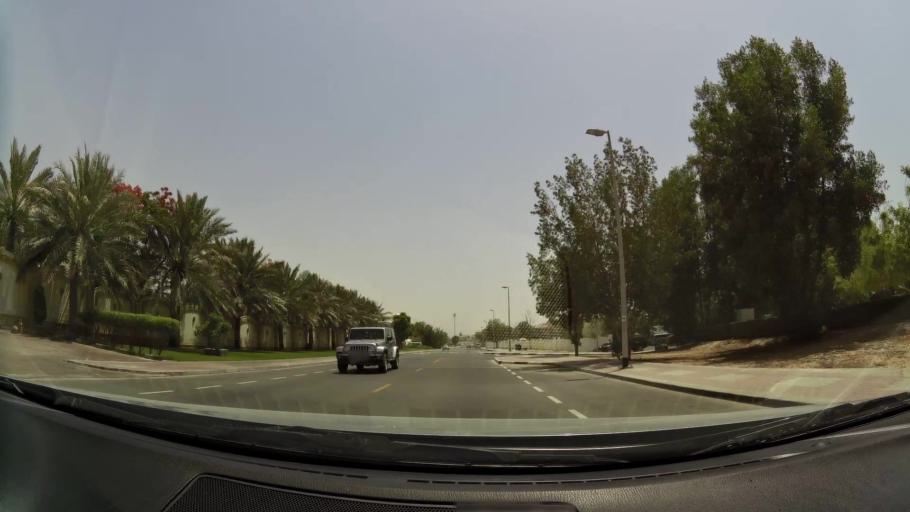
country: AE
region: Dubai
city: Dubai
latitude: 25.1481
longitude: 55.2066
